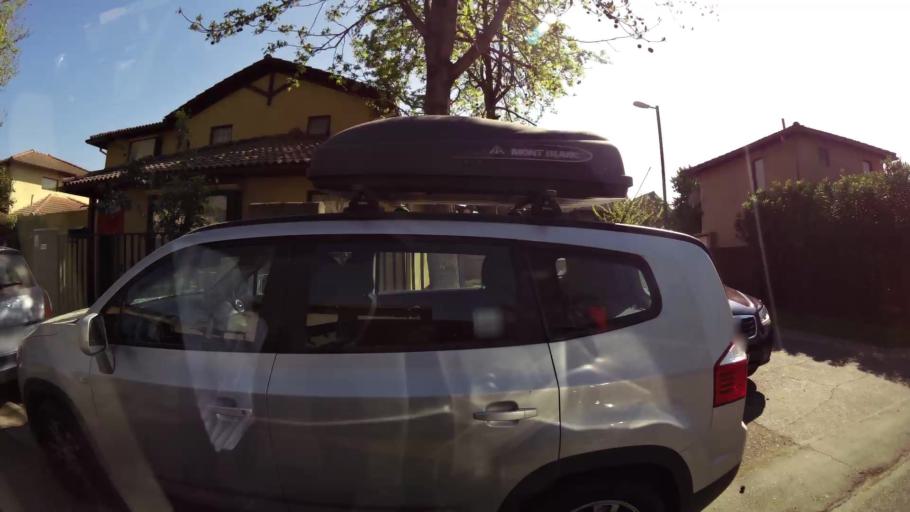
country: CL
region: Santiago Metropolitan
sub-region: Provincia de Chacabuco
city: Chicureo Abajo
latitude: -33.3571
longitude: -70.6801
